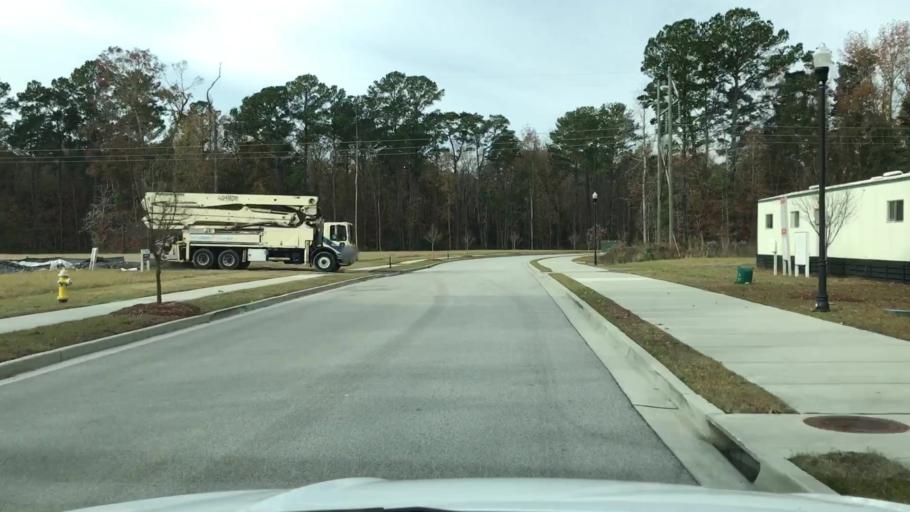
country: US
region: South Carolina
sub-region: Charleston County
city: Shell Point
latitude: 32.8058
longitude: -80.0586
